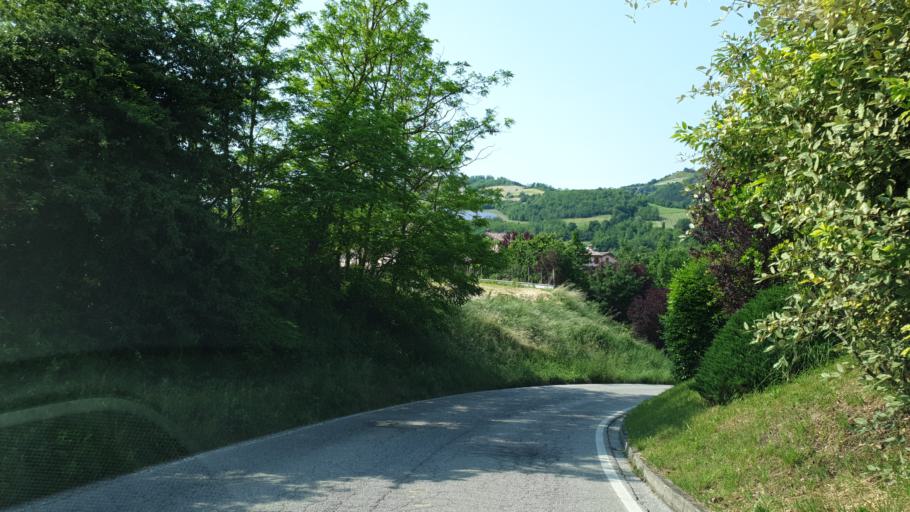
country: IT
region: Emilia-Romagna
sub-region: Forli-Cesena
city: Sarsina
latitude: 43.9210
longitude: 12.1643
